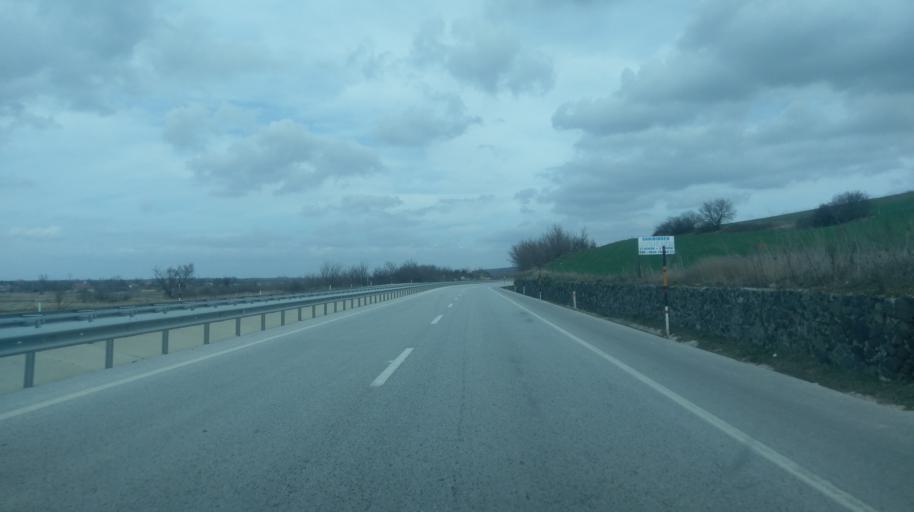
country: TR
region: Edirne
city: Uzun Keupru
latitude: 41.3013
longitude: 26.6996
